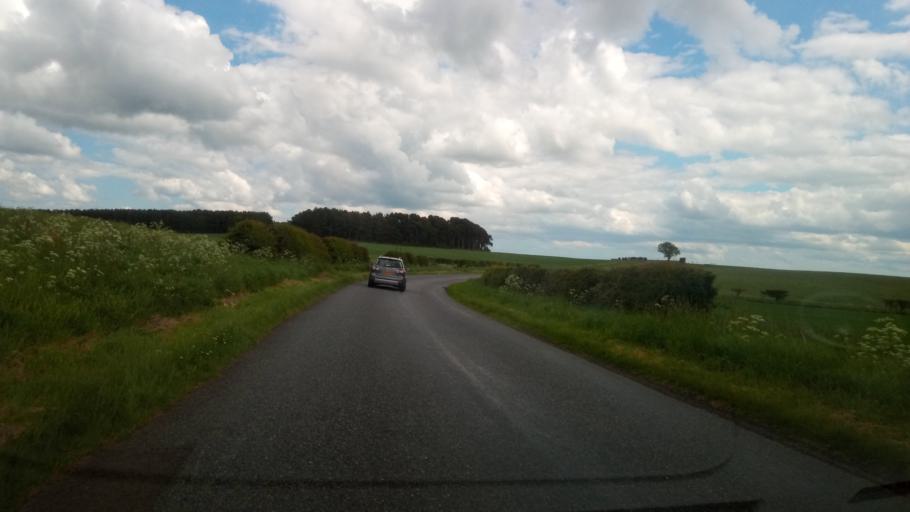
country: GB
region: Scotland
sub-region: The Scottish Borders
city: Kelso
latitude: 55.5965
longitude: -2.3568
